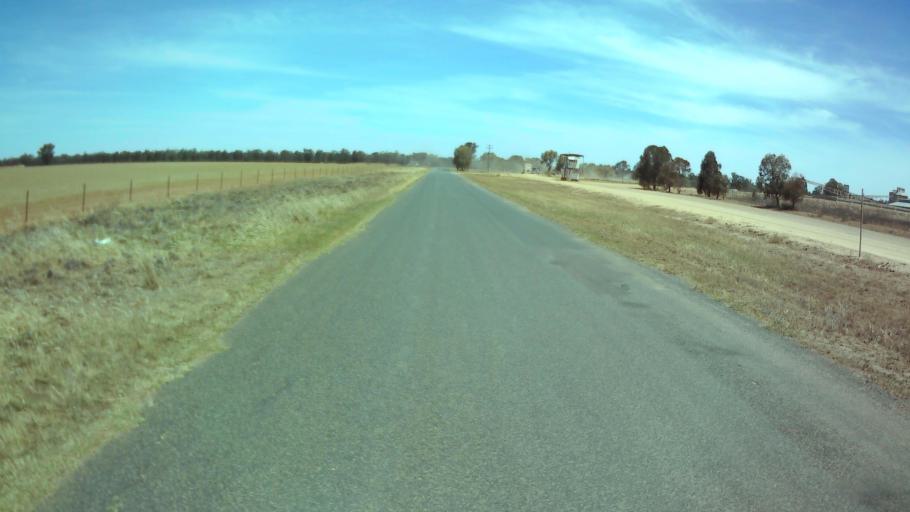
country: AU
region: New South Wales
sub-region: Weddin
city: Grenfell
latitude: -33.8328
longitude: 147.7457
